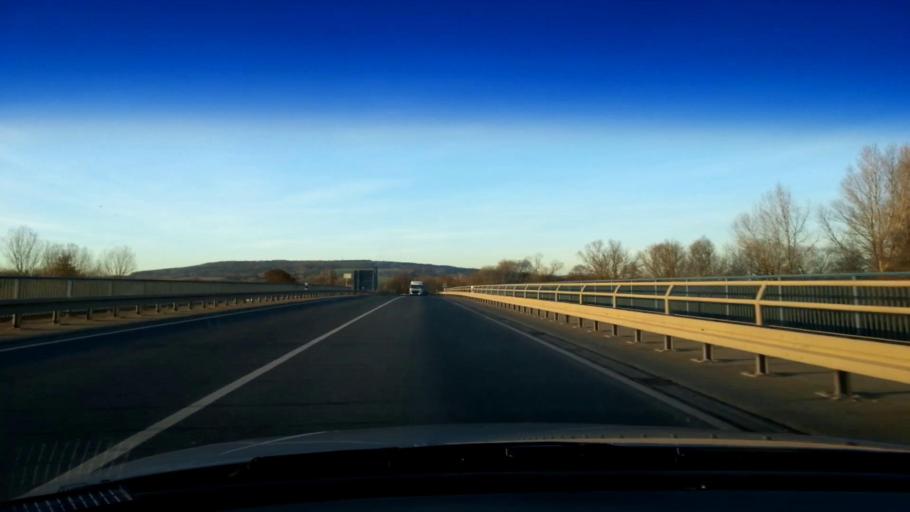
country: DE
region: Bavaria
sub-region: Upper Franconia
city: Breitengussbach
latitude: 49.9809
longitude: 10.8852
